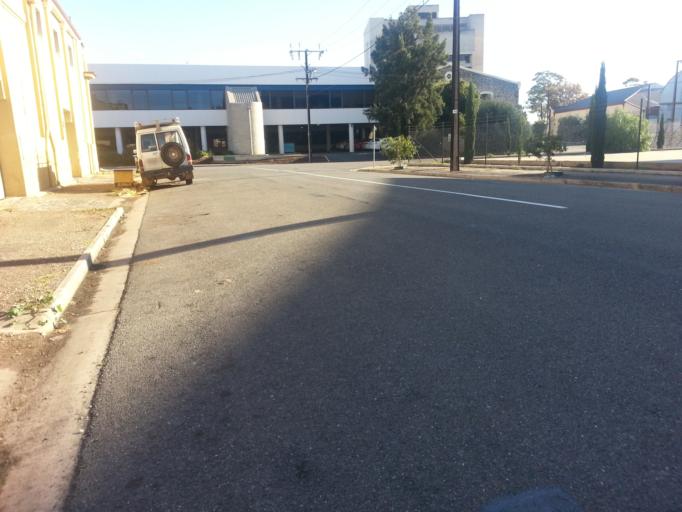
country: AU
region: South Australia
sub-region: Port Adelaide Enfield
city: Birkenhead
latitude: -34.8449
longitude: 138.5094
